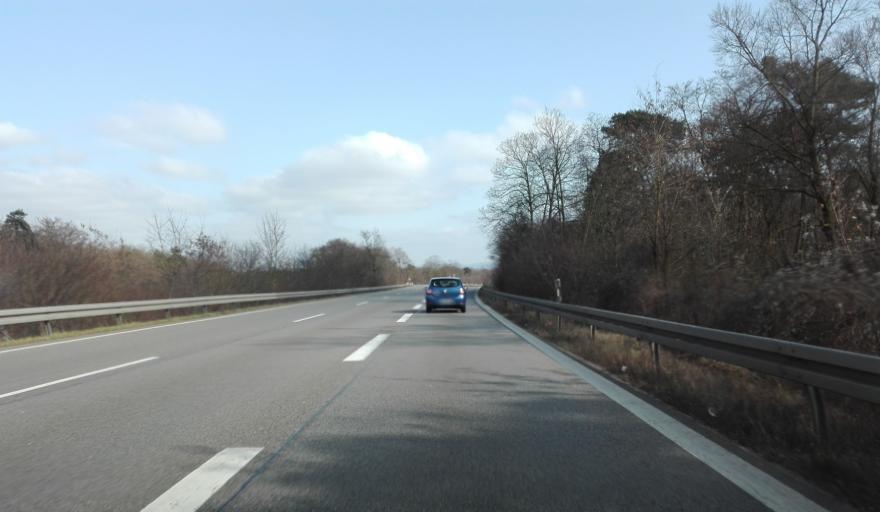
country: DE
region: Hesse
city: Viernheim
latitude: 49.5558
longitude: 8.5480
